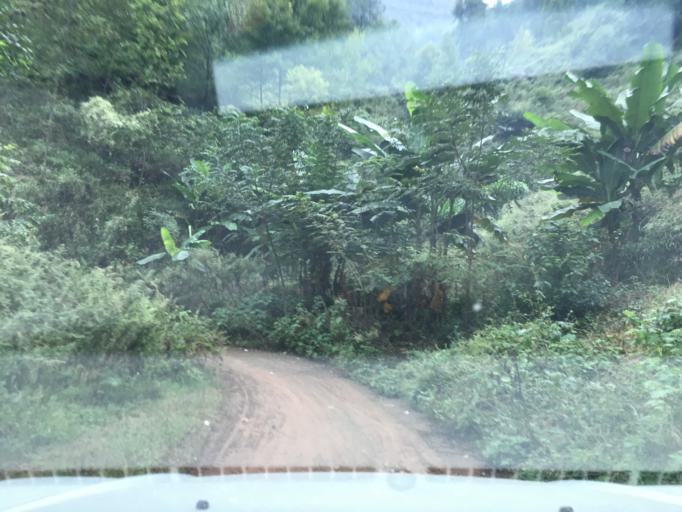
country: CN
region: Guizhou Sheng
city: Liupanshui
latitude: 26.0729
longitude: 105.0680
